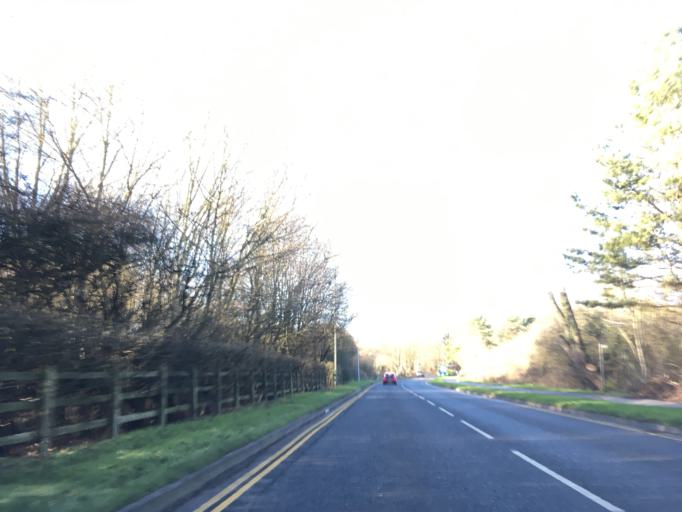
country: GB
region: England
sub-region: Borough of Swindon
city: Swindon
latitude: 51.5387
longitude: -1.7789
